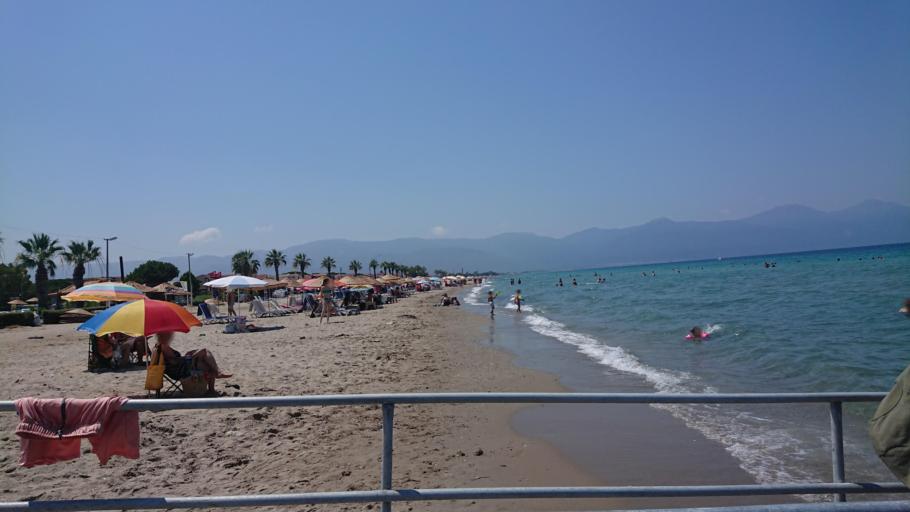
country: TR
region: Aydin
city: Kusadasi
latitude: 37.7954
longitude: 27.2680
